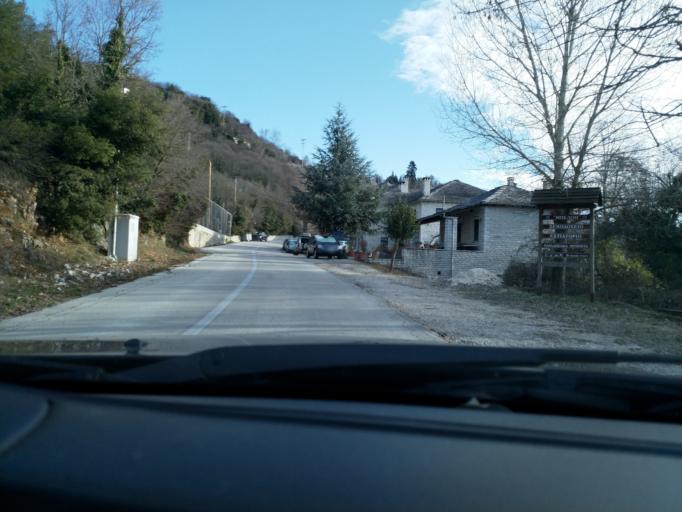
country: GR
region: Epirus
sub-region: Nomos Ioanninon
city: Asprangeloi
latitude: 39.8725
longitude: 20.7455
